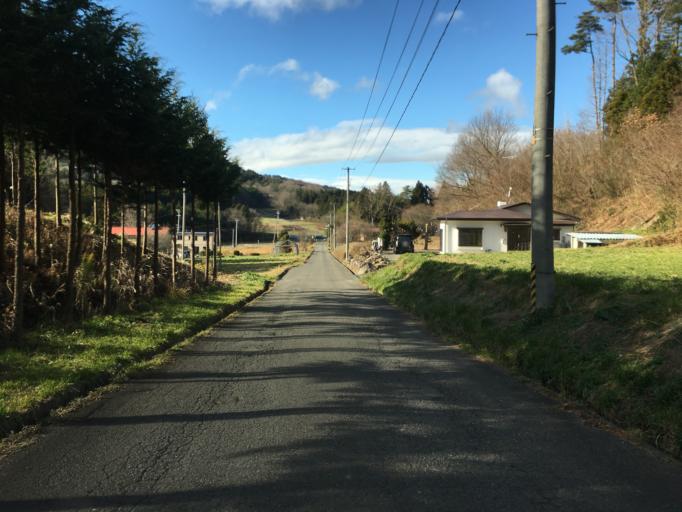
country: JP
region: Fukushima
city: Ishikawa
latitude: 37.2645
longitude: 140.5573
